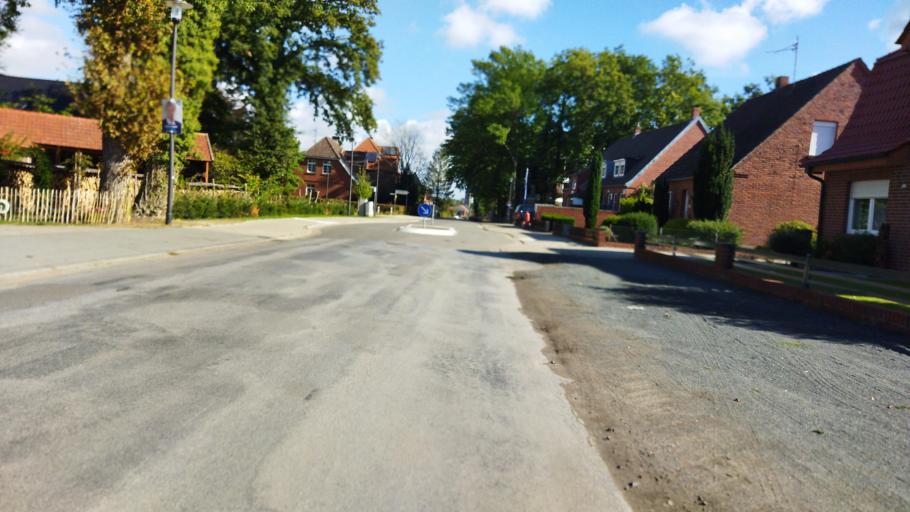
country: DE
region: Lower Saxony
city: Salzbergen
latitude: 52.3181
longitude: 7.3372
